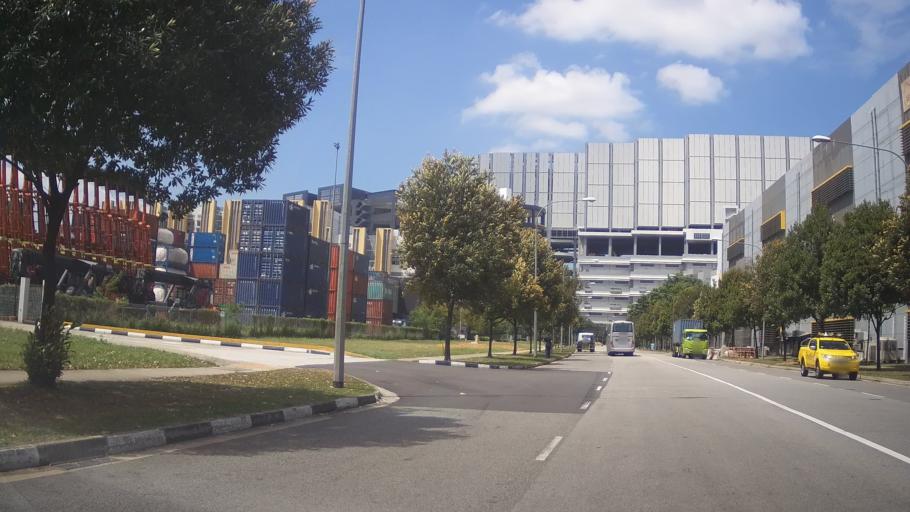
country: SG
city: Singapore
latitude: 1.3130
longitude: 103.7015
